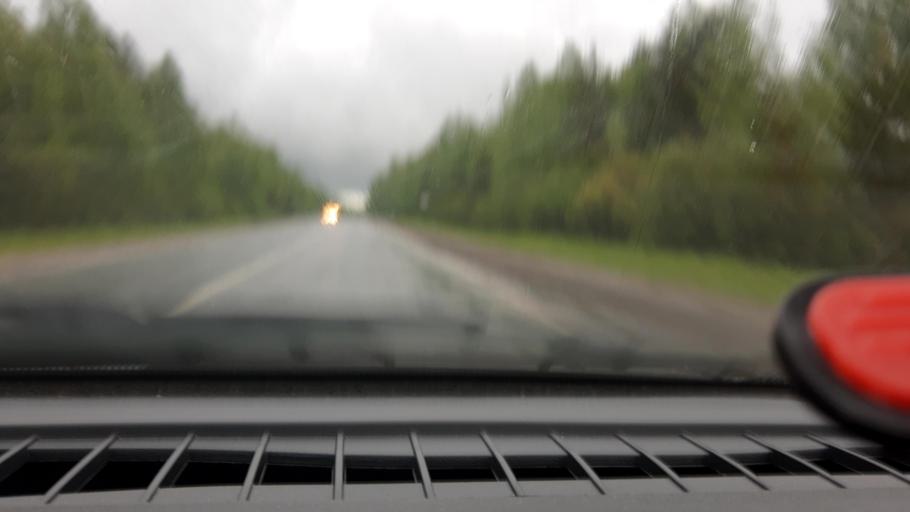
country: RU
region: Nizjnij Novgorod
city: Semenov
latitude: 56.7766
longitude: 44.4269
